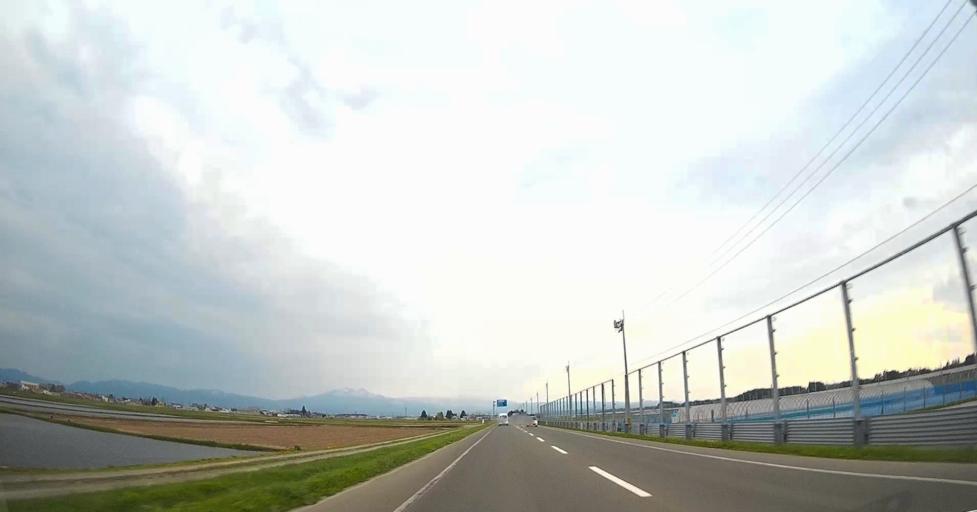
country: JP
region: Aomori
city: Aomori Shi
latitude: 40.8750
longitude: 140.6729
